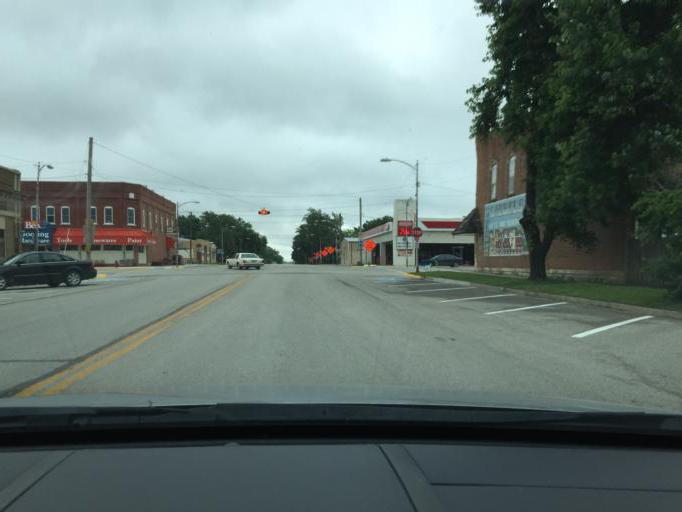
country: US
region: Kansas
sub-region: McPherson County
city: Moundridge
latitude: 38.2030
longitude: -97.5197
